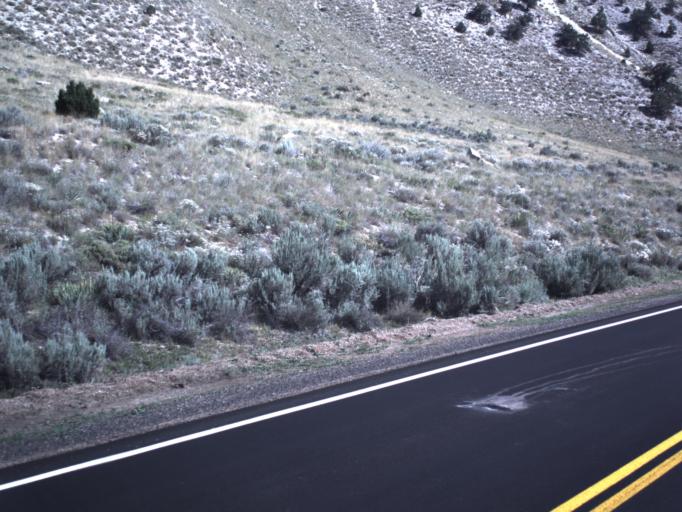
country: US
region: Utah
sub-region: Duchesne County
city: Duchesne
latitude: 39.9879
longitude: -110.6023
